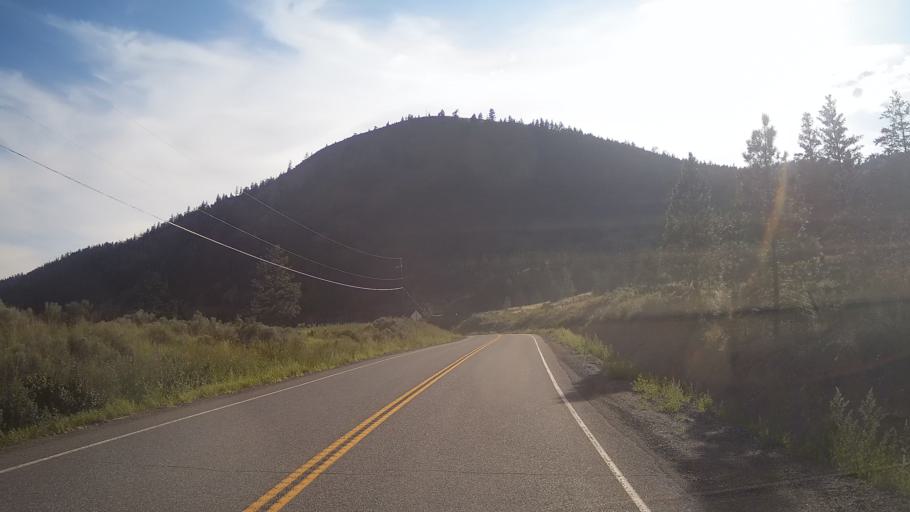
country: CA
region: British Columbia
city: Cache Creek
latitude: 50.8770
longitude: -121.5145
